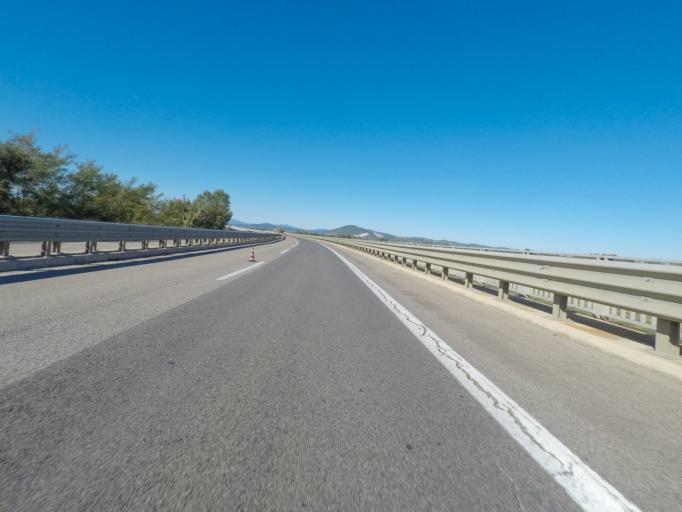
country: IT
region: Tuscany
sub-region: Provincia di Grosseto
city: Grosseto
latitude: 42.7482
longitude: 11.1441
